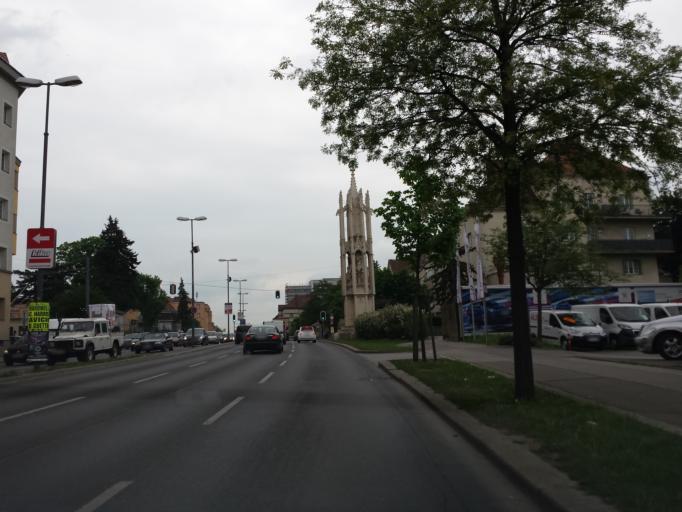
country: AT
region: Vienna
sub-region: Wien Stadt
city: Vienna
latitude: 48.1715
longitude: 16.3512
